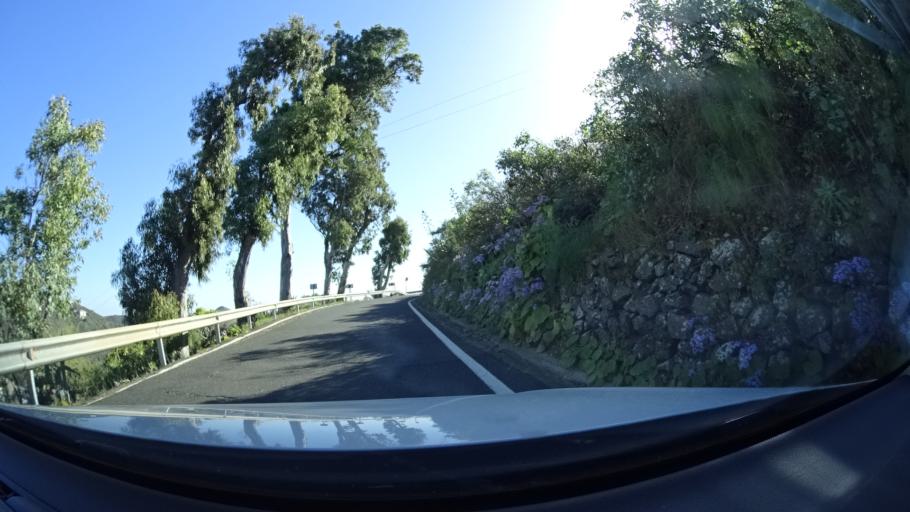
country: ES
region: Canary Islands
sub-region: Provincia de Las Palmas
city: Santa Brigida
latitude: 28.0191
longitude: -15.4650
